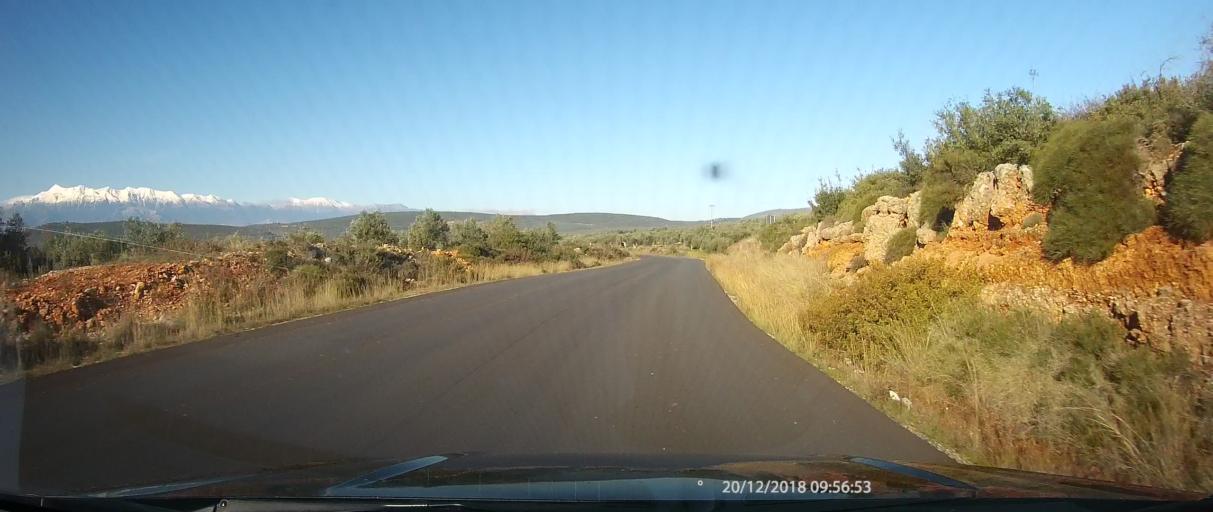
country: GR
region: Peloponnese
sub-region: Nomos Lakonias
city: Yerakion
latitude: 37.0202
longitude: 22.6059
